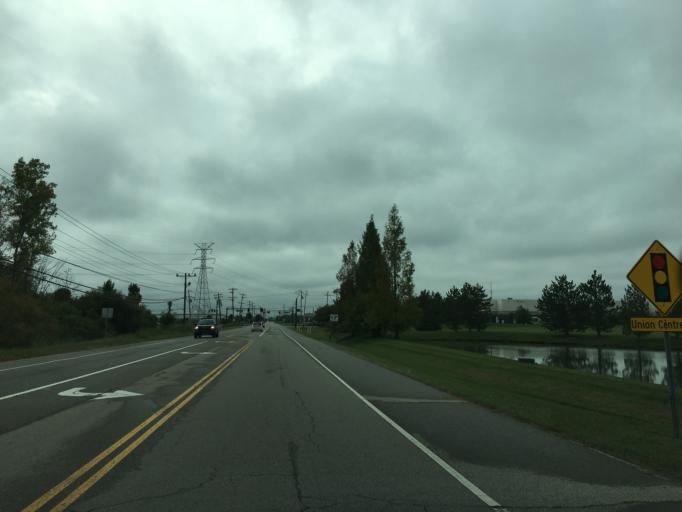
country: US
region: Ohio
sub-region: Butler County
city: Beckett Ridge
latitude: 39.3407
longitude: -84.4438
